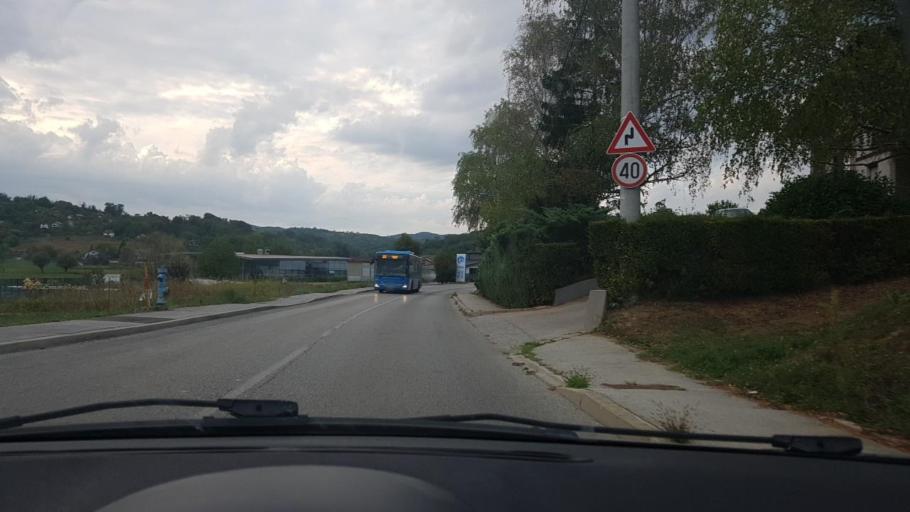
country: HR
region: Grad Zagreb
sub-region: Sesvete
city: Sesvete
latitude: 45.9012
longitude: 16.1634
